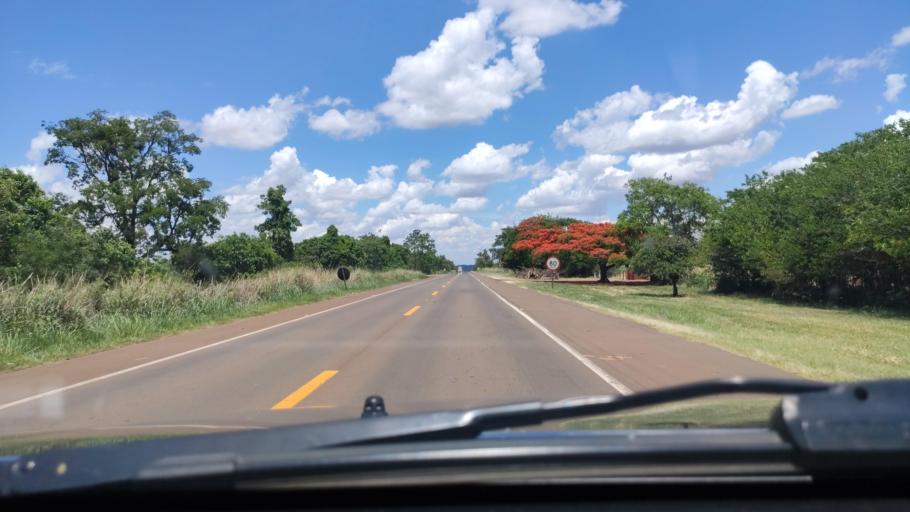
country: BR
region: Sao Paulo
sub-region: Boa Esperanca Do Sul
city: Boa Esperanca do Sul
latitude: -22.0695
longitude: -48.4025
